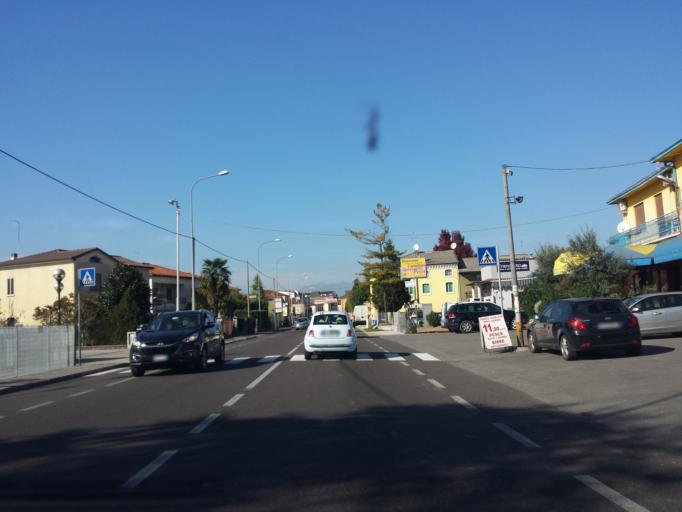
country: IT
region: Veneto
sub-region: Provincia di Vicenza
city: Crispi Cavour
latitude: 45.5726
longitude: 11.5128
